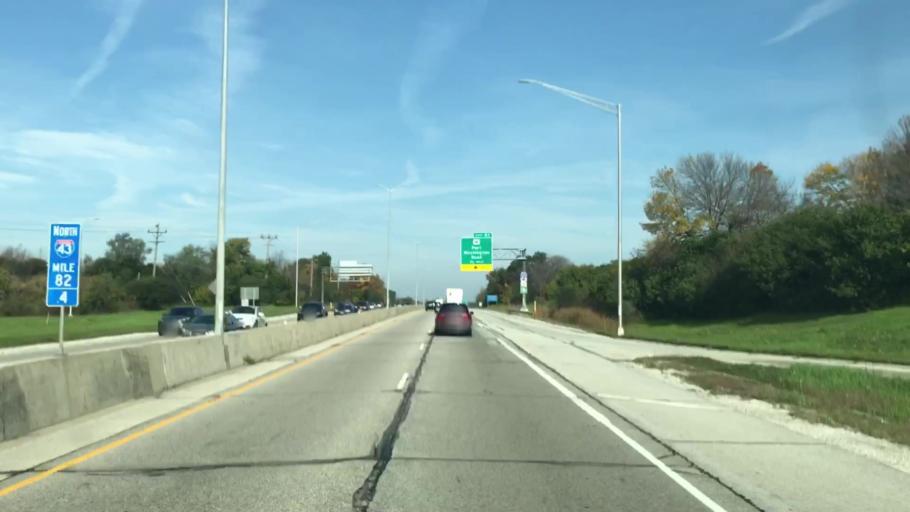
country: US
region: Wisconsin
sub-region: Milwaukee County
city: River Hills
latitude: 43.1784
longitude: -87.9179
